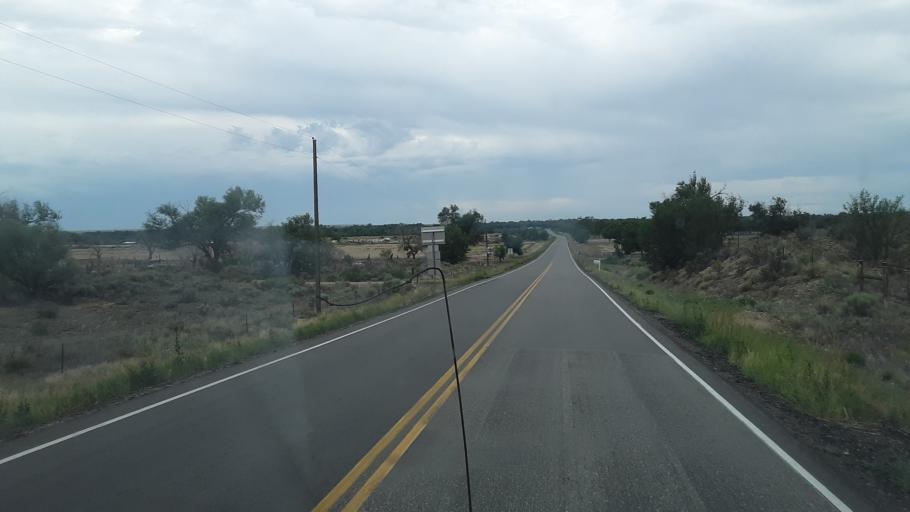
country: US
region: Colorado
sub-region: Otero County
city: Fowler
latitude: 38.1542
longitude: -104.0232
